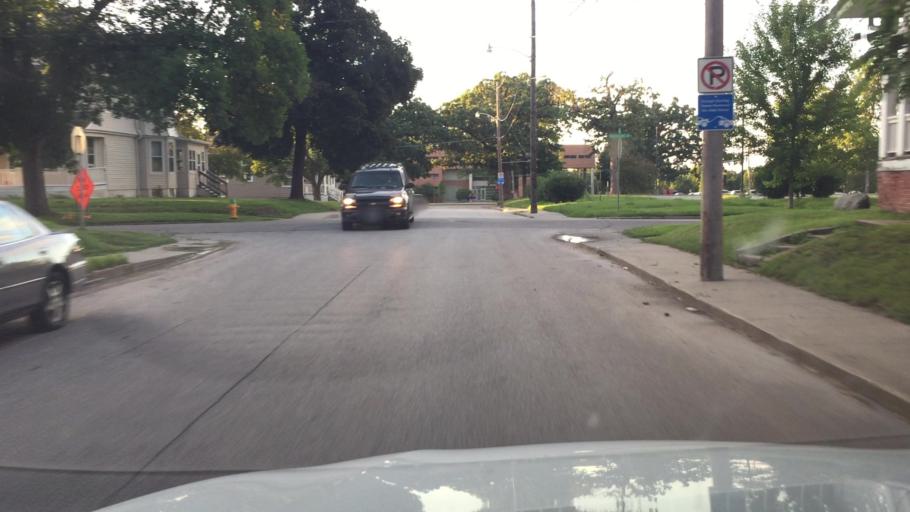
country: US
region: Iowa
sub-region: Polk County
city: Des Moines
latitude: 41.5992
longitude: -93.6569
